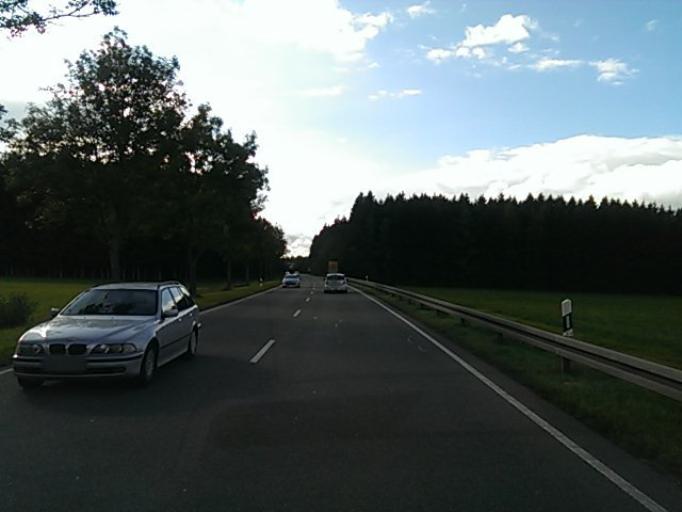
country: DE
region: Baden-Wuerttemberg
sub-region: Freiburg Region
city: Talheim
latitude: 48.0252
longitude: 8.6404
